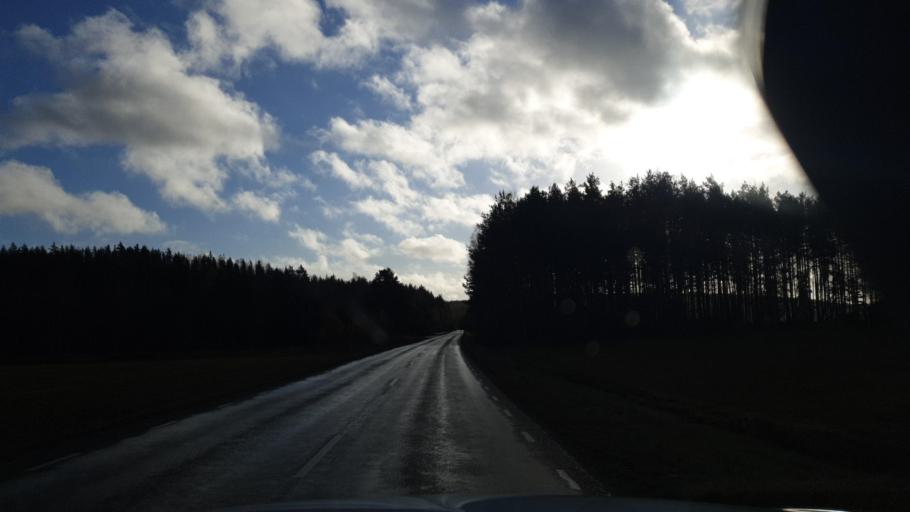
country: SE
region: Vaermland
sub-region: Grums Kommun
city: Slottsbron
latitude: 59.4101
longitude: 12.9998
